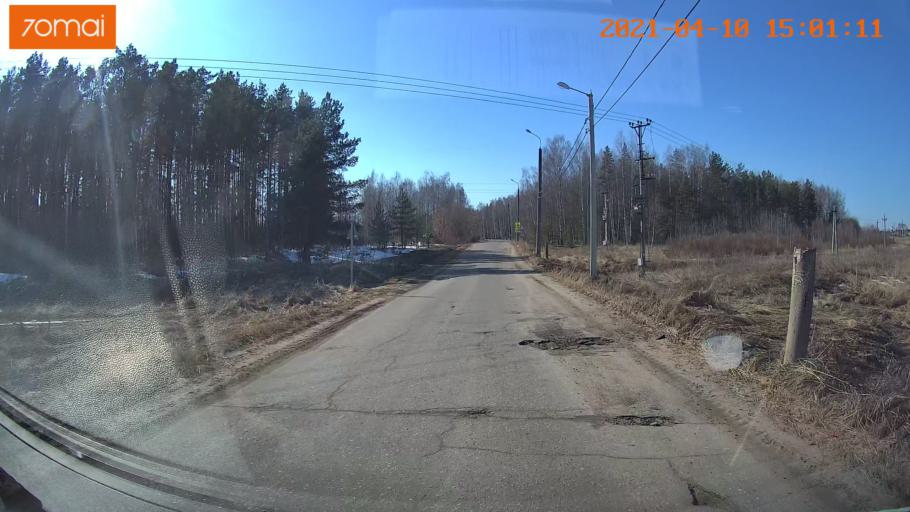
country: RU
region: Ivanovo
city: Bogorodskoye
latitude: 56.9979
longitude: 41.0590
